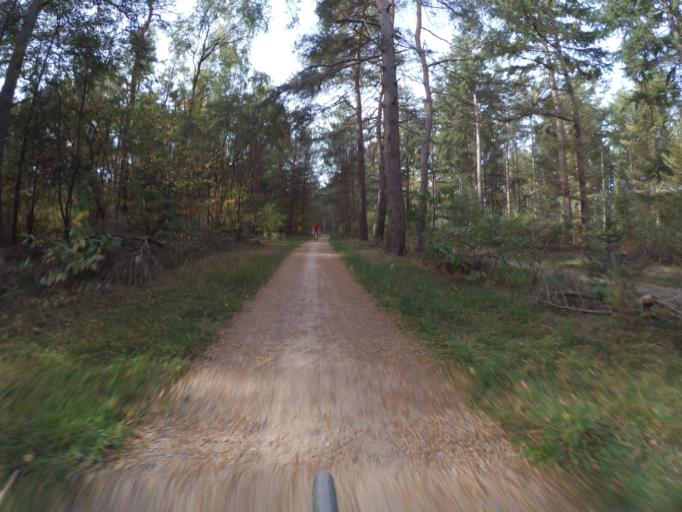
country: NL
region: Overijssel
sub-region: Gemeente Raalte
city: Raalte
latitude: 52.3601
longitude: 6.4069
